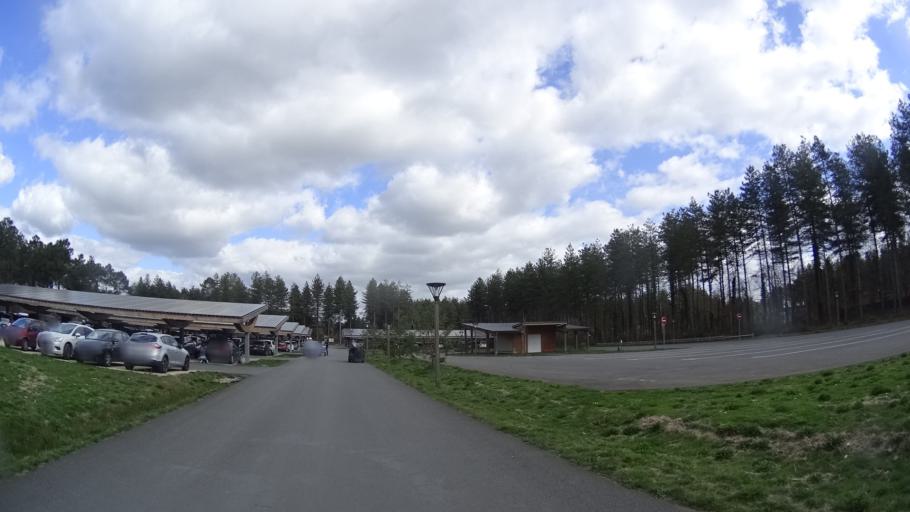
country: FR
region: Pays de la Loire
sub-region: Departement de Maine-et-Loire
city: Fontevraud-l'Abbaye
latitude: 47.0917
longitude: 0.0035
